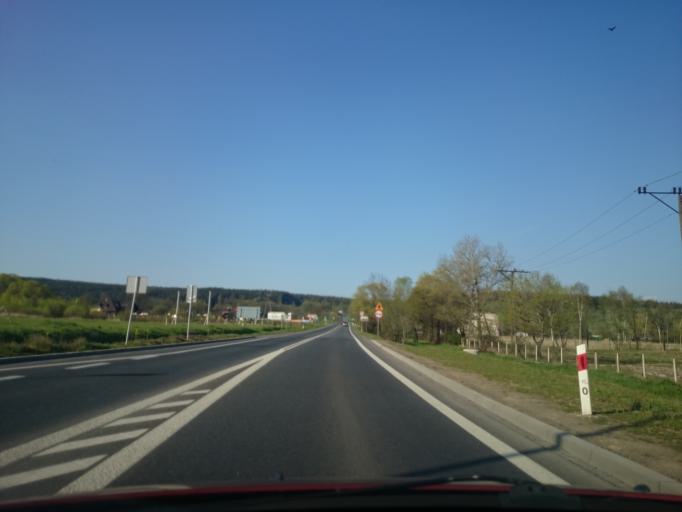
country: PL
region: Lower Silesian Voivodeship
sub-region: Powiat klodzki
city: Szczytna
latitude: 50.4151
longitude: 16.4489
